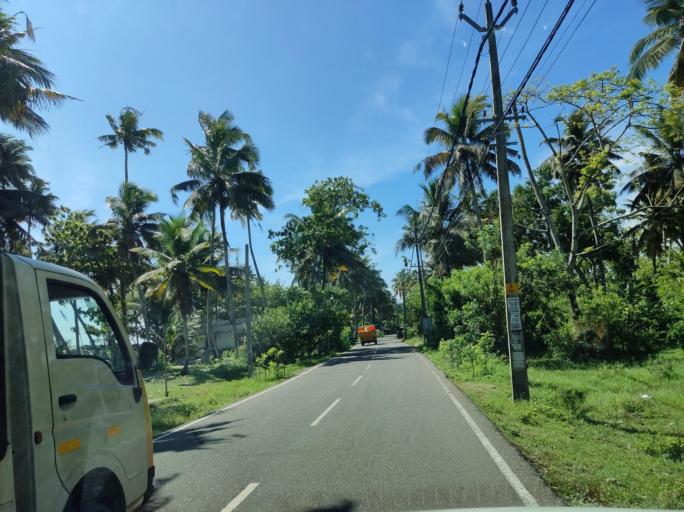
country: IN
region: Kerala
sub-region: Alappuzha
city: Kayankulam
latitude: 9.1767
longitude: 76.4451
